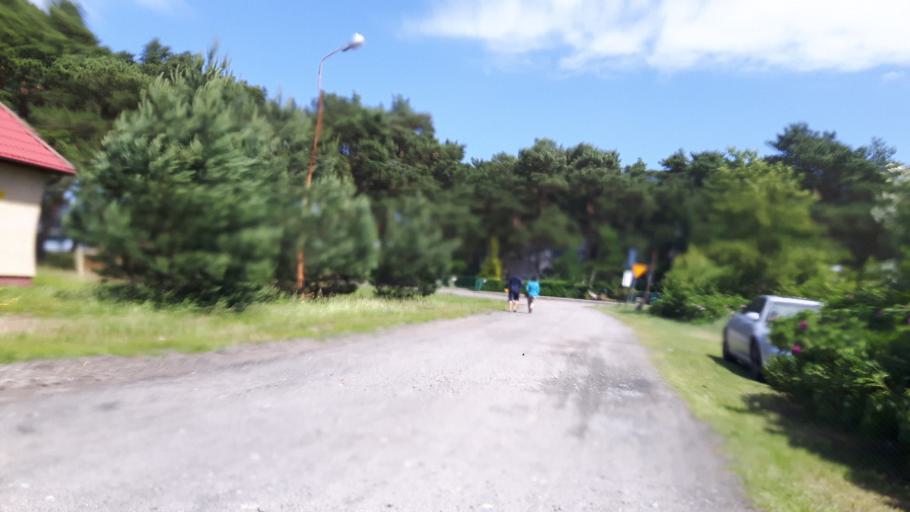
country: PL
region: West Pomeranian Voivodeship
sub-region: Powiat gryficki
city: Mrzezyno
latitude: 54.1421
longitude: 15.3025
